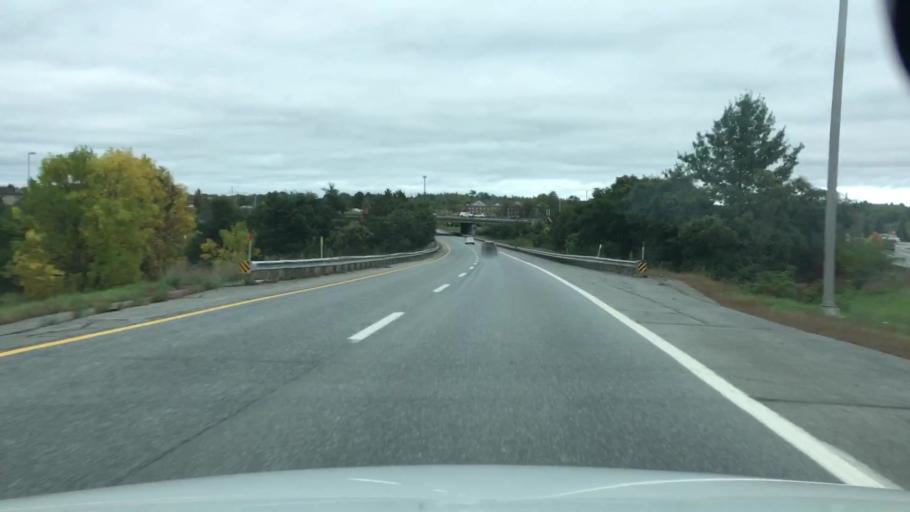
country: US
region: Maine
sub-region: Penobscot County
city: Brewer
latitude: 44.8300
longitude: -68.7439
